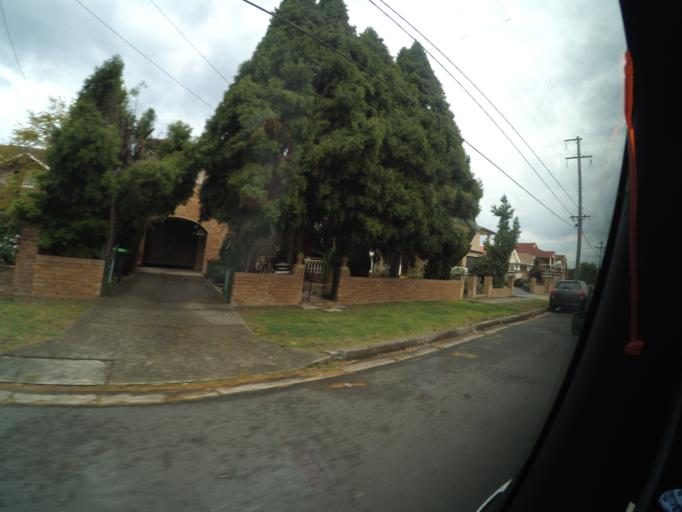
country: AU
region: New South Wales
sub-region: Bankstown
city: Bankstown
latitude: -33.9275
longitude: 151.0280
